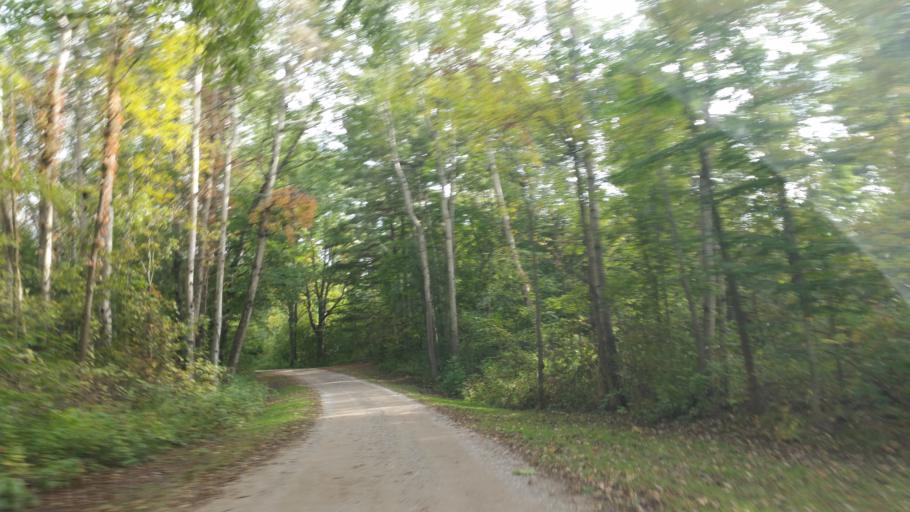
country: CA
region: Ontario
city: Delaware
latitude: 42.8756
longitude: -81.4782
